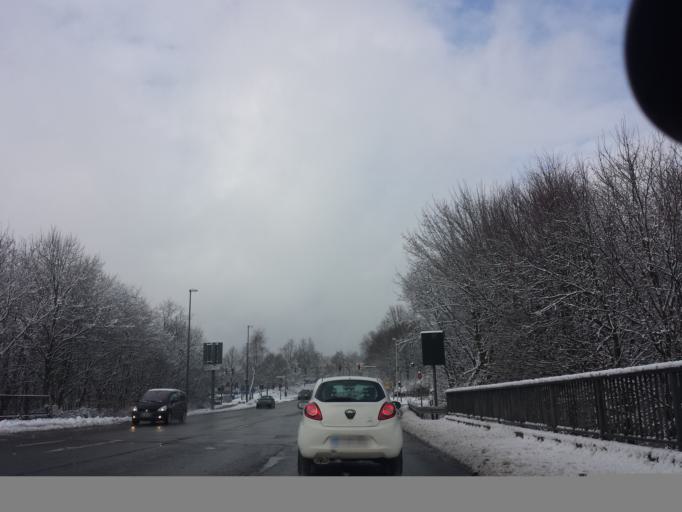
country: DE
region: North Rhine-Westphalia
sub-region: Regierungsbezirk Dusseldorf
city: Wuppertal
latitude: 51.2268
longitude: 7.1471
